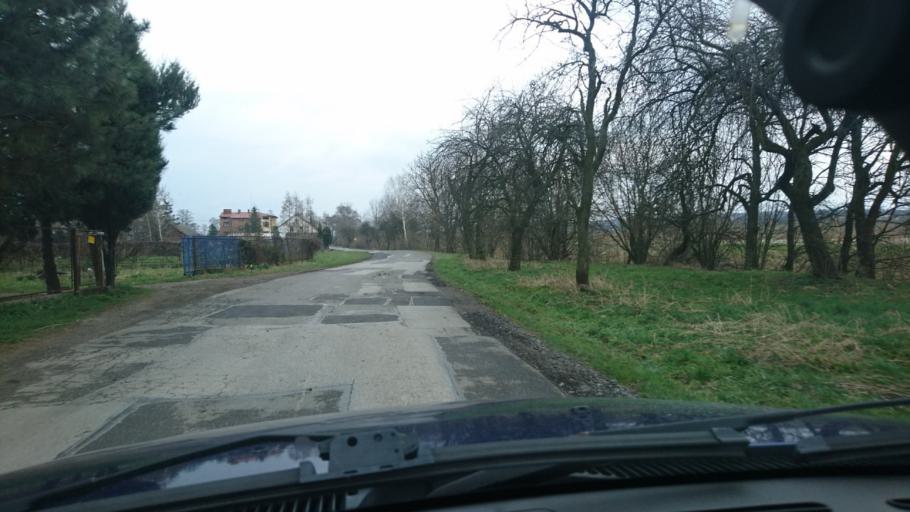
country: PL
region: Silesian Voivodeship
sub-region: Powiat bielski
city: Bronow
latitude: 49.8779
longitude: 18.8857
